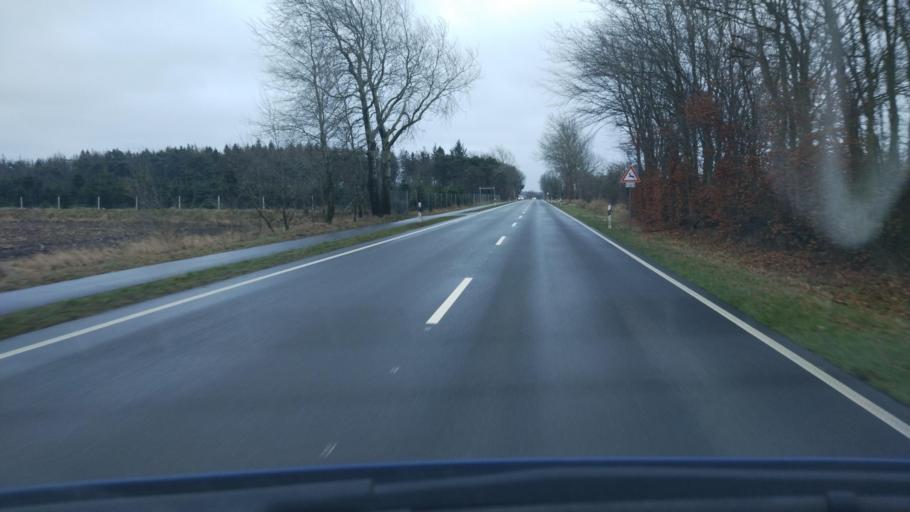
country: DE
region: Schleswig-Holstein
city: Klein Rheide
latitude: 54.4298
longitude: 9.4901
